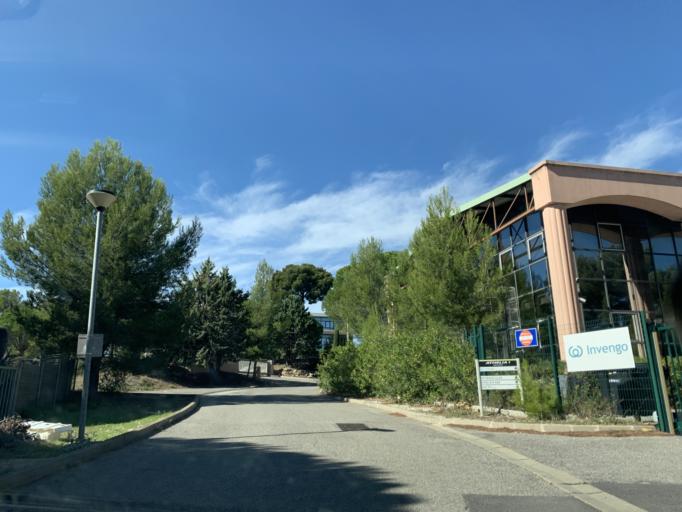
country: FR
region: Provence-Alpes-Cote d'Azur
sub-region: Departement des Bouches-du-Rhone
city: La Ciotat
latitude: 43.2016
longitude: 5.5931
